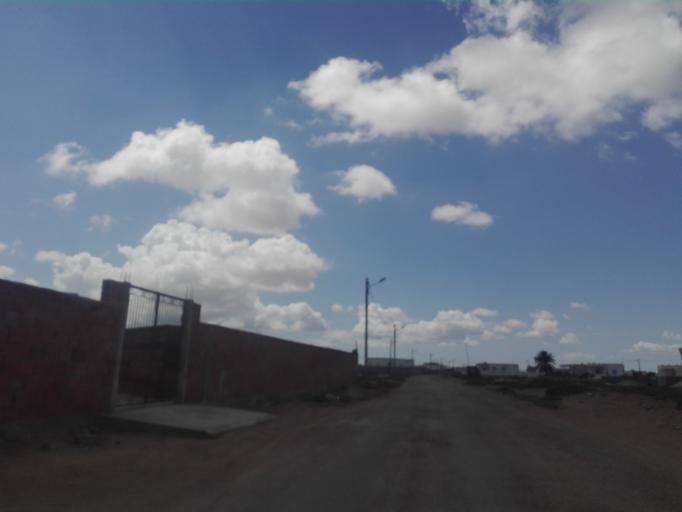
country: TN
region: Safaqis
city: Jabinyanah
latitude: 34.8249
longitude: 11.2538
